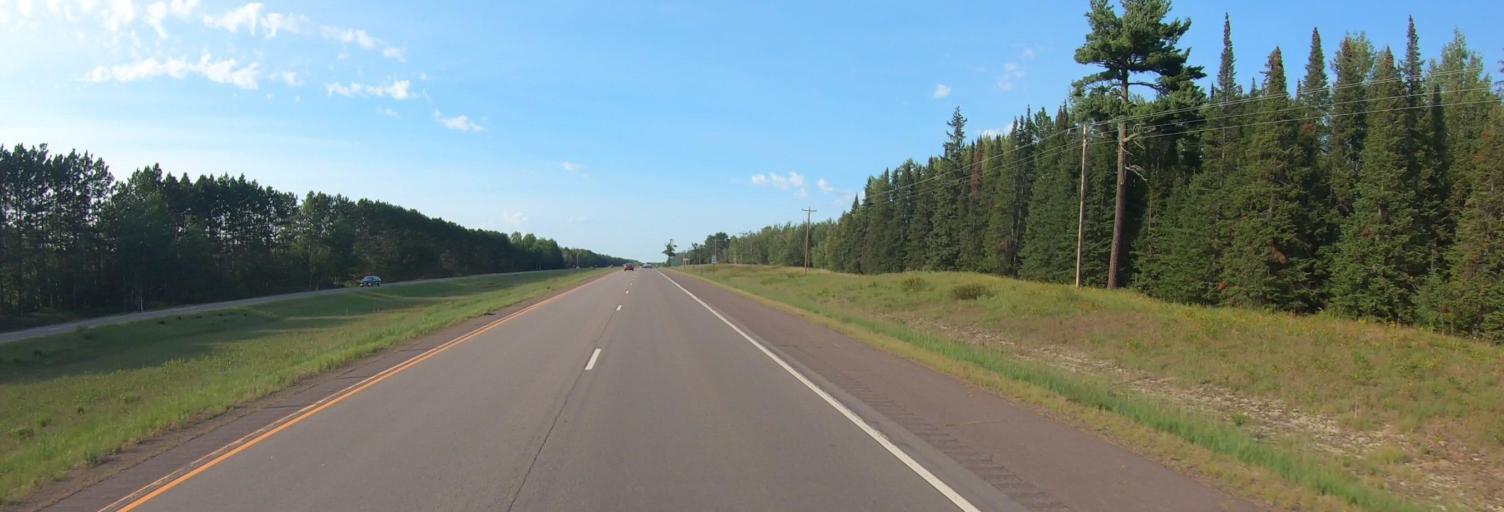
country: US
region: Minnesota
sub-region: Saint Louis County
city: Eveleth
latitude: 47.0998
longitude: -92.4713
